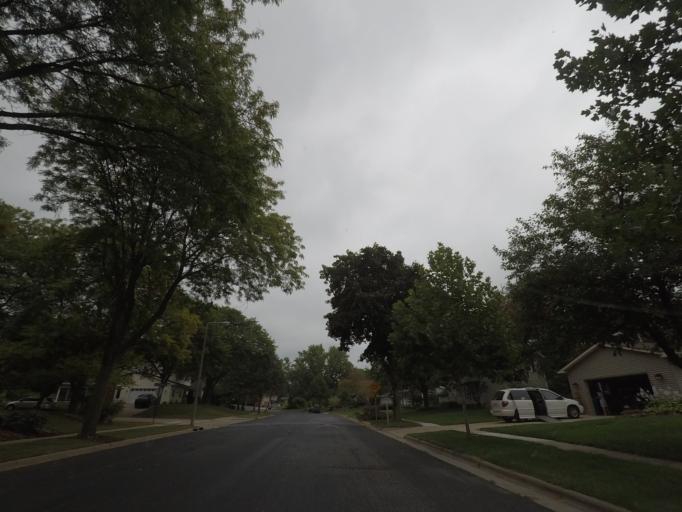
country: US
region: Wisconsin
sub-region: Dane County
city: Middleton
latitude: 43.0913
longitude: -89.5133
